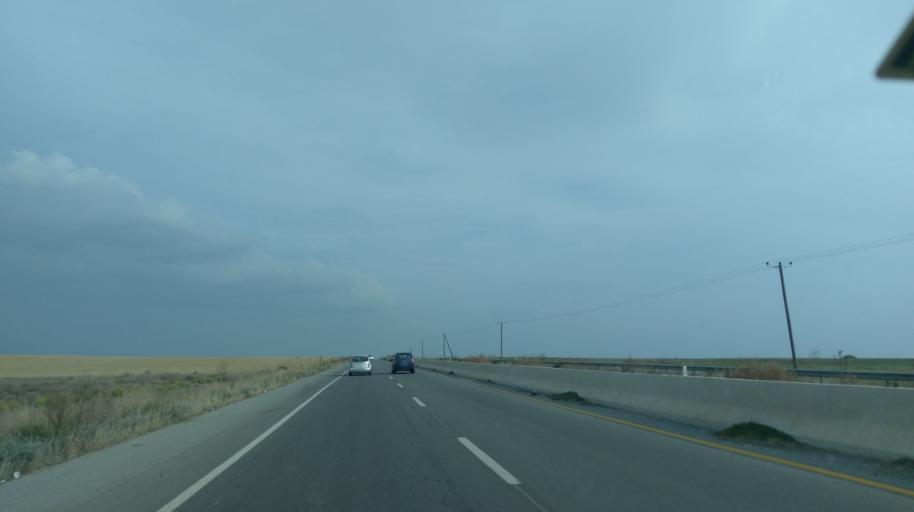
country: CY
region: Lefkosia
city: Mammari
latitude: 35.2128
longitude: 33.2001
